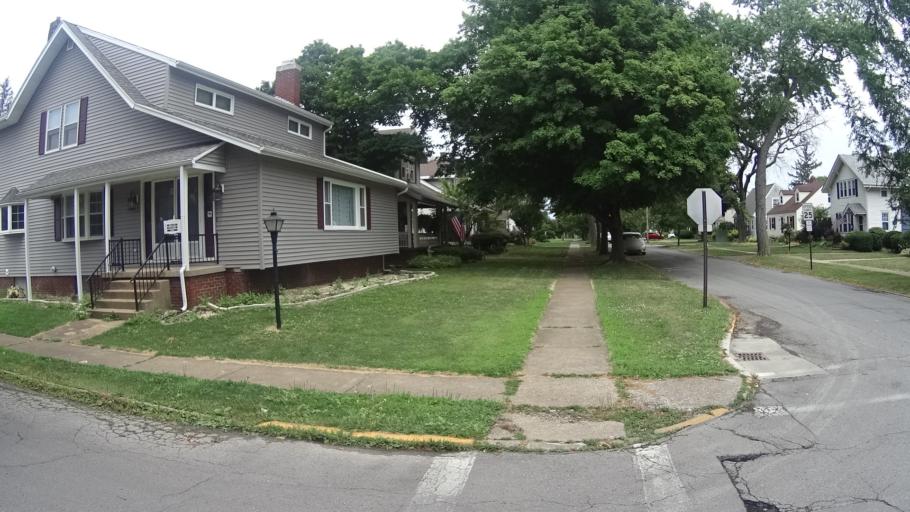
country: US
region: Ohio
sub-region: Erie County
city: Sandusky
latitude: 41.4365
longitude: -82.6963
